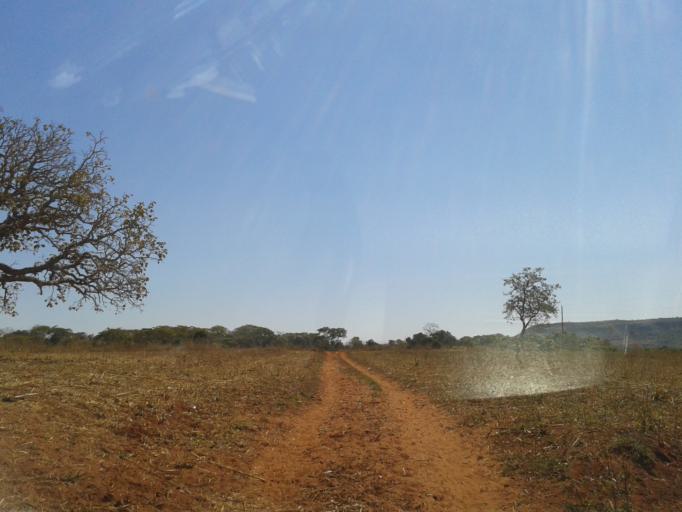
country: BR
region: Minas Gerais
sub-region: Santa Vitoria
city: Santa Vitoria
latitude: -19.0774
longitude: -50.0318
